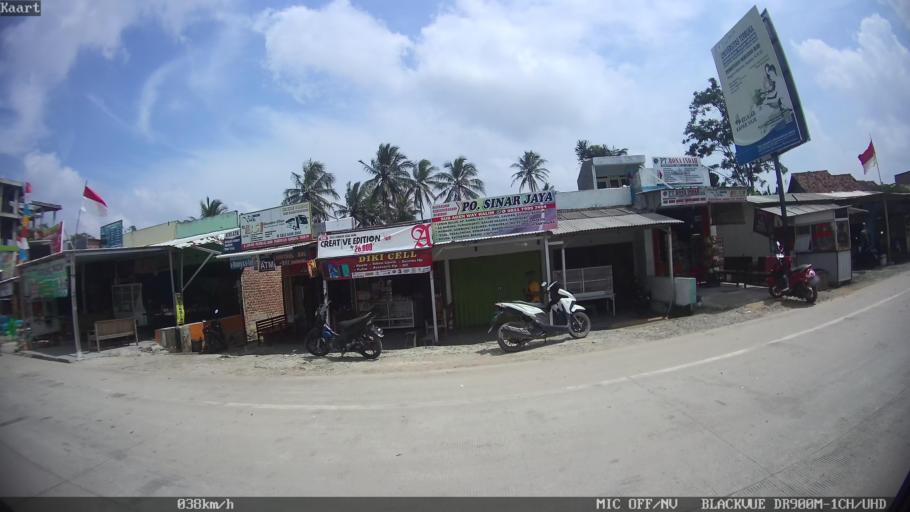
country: ID
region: Lampung
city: Kedaton
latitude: -5.3522
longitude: 105.3245
